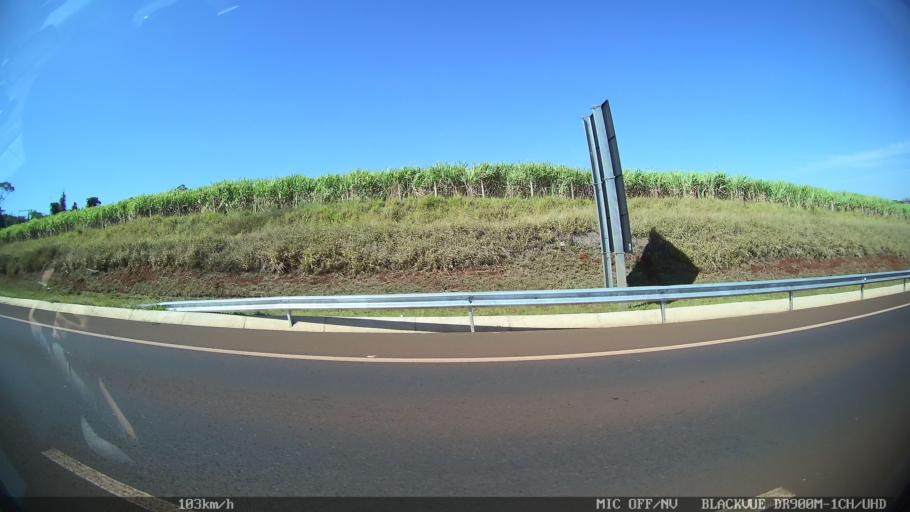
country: BR
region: Sao Paulo
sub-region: Franca
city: Franca
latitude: -20.6538
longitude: -47.4886
